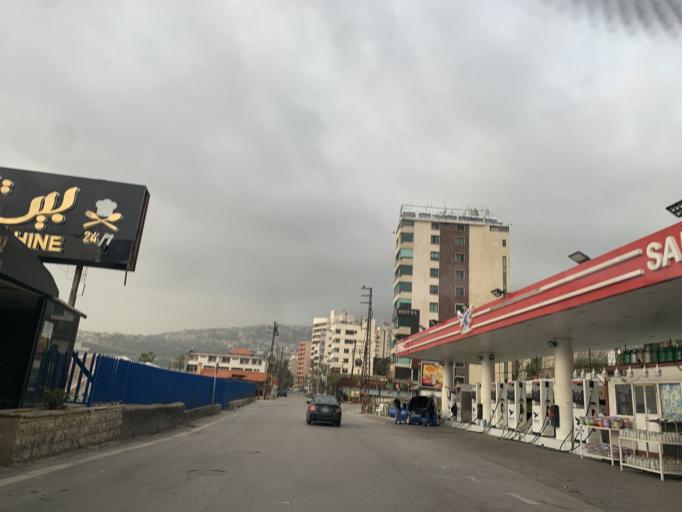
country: LB
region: Mont-Liban
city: Djounie
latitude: 34.0002
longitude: 35.6443
